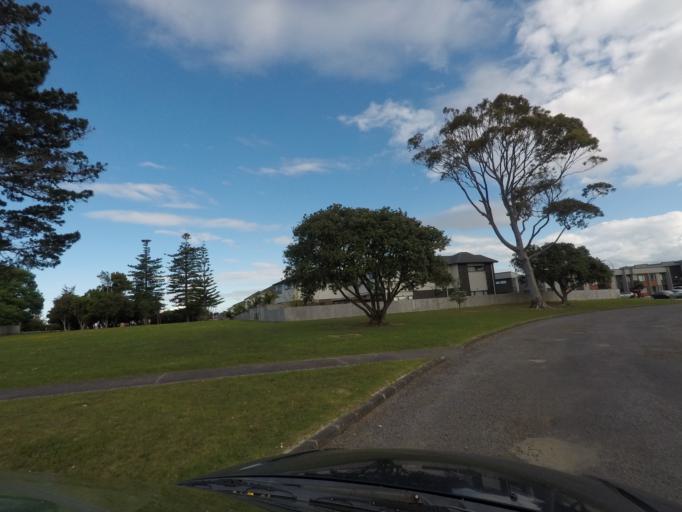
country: NZ
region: Auckland
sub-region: Auckland
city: Rosebank
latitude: -36.8729
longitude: 174.6441
